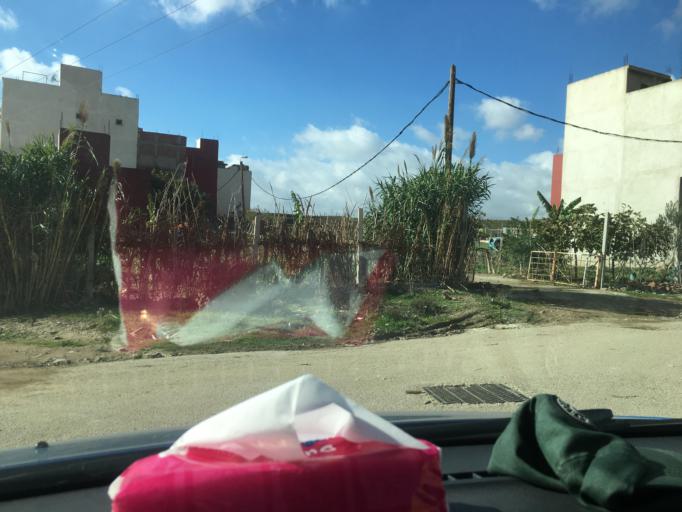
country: MA
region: Tanger-Tetouan
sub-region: Tanger-Assilah
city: Tangier
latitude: 35.7246
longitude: -5.8152
